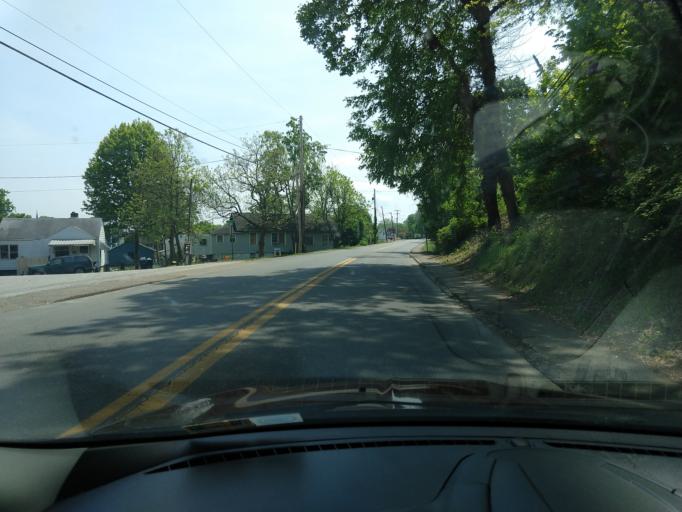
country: US
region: West Virginia
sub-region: Kanawha County
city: Saint Albans
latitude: 38.3800
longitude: -81.8210
